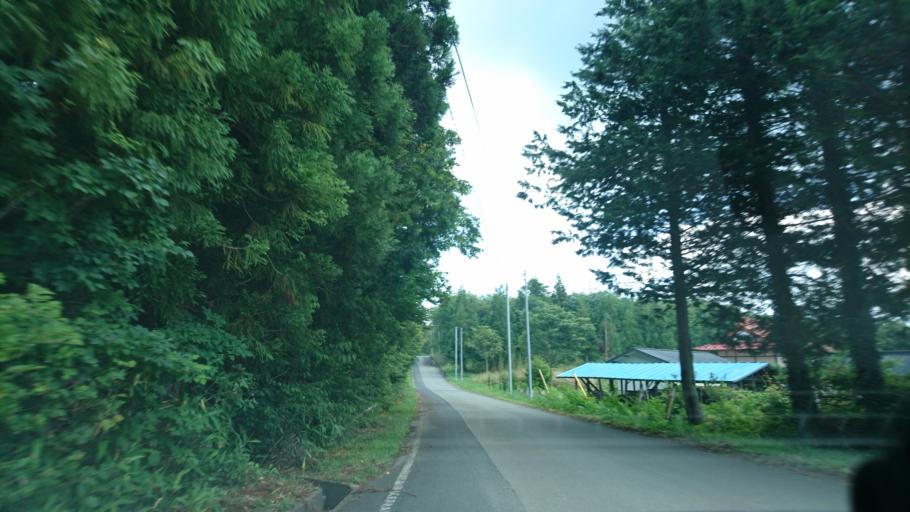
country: JP
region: Iwate
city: Ichinoseki
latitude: 38.9133
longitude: 141.2130
